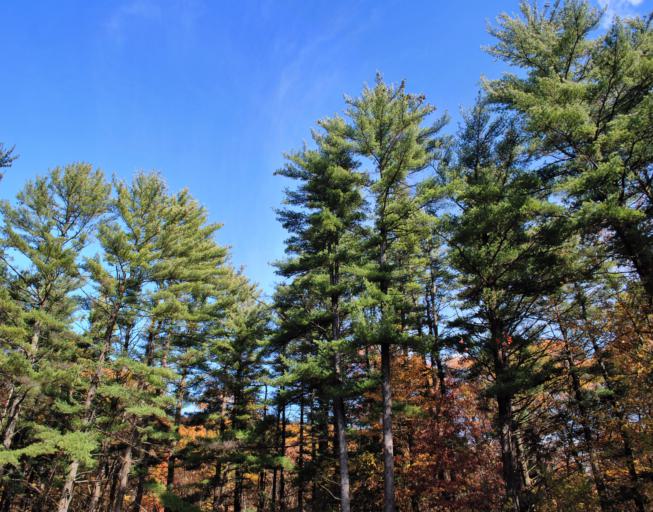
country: US
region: Wisconsin
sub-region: Sauk County
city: Baraboo
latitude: 43.4110
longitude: -89.7106
